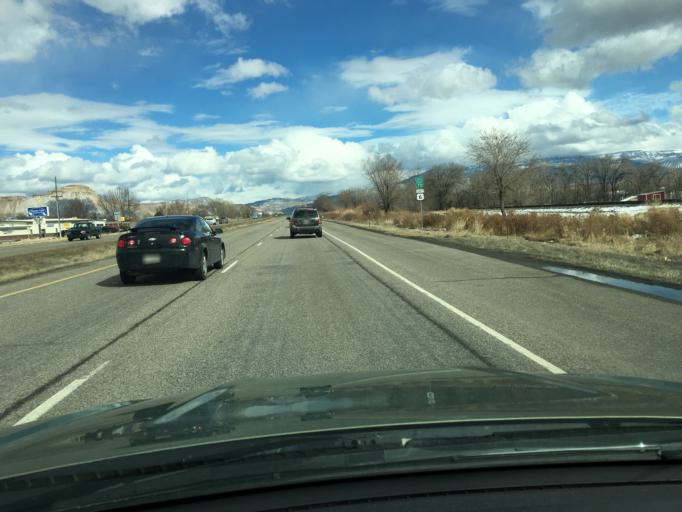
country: US
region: Colorado
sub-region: Mesa County
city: Fruitvale
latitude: 39.0782
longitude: -108.4914
